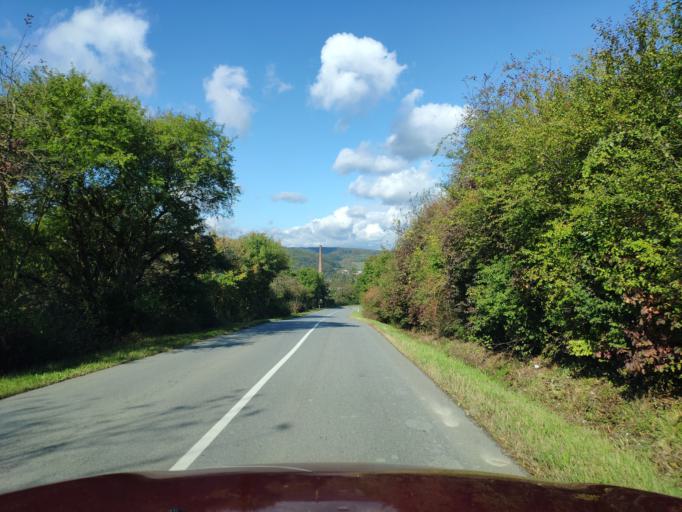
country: SK
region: Presovsky
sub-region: Okres Presov
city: Presov
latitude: 48.8880
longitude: 21.2627
